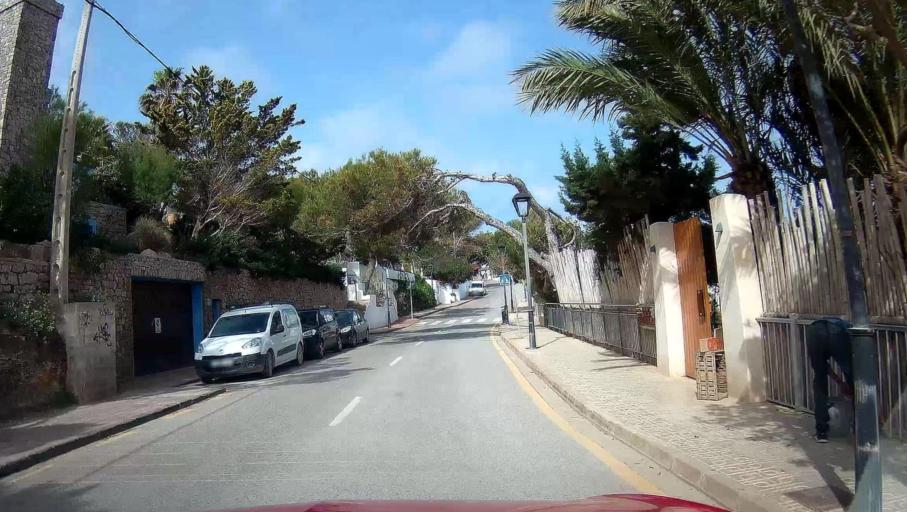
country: ES
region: Balearic Islands
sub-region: Illes Balears
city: Sant Joan de Labritja
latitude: 39.1135
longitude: 1.5198
